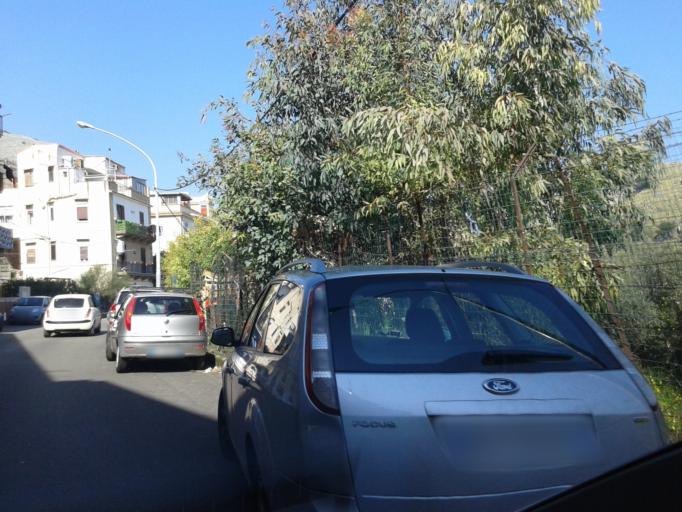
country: IT
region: Sicily
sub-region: Palermo
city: Piano dei Geli
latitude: 38.1144
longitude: 13.2951
